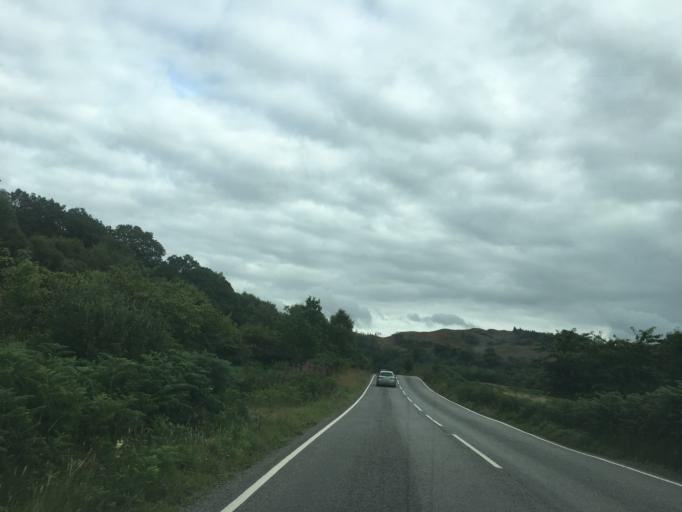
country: GB
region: Scotland
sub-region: Argyll and Bute
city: Oban
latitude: 56.3243
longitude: -5.4999
